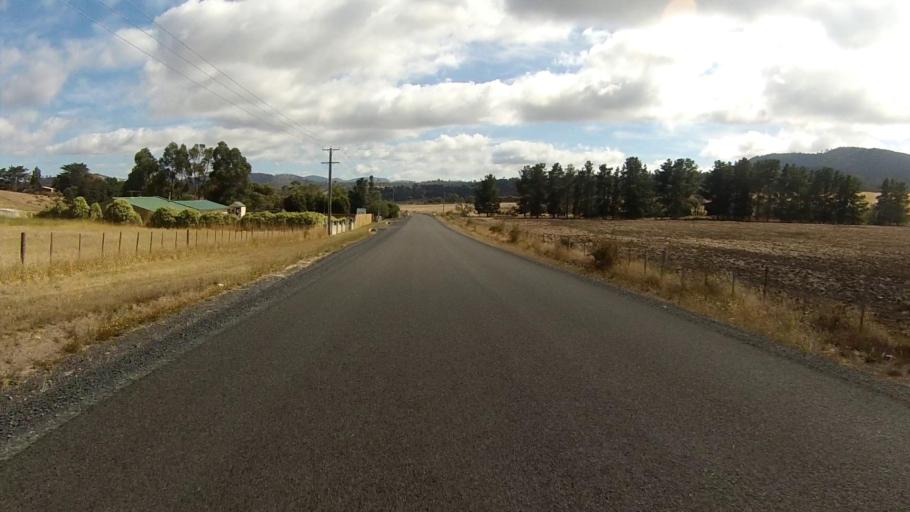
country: AU
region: Tasmania
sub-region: Brighton
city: Old Beach
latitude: -42.7644
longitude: 147.3000
